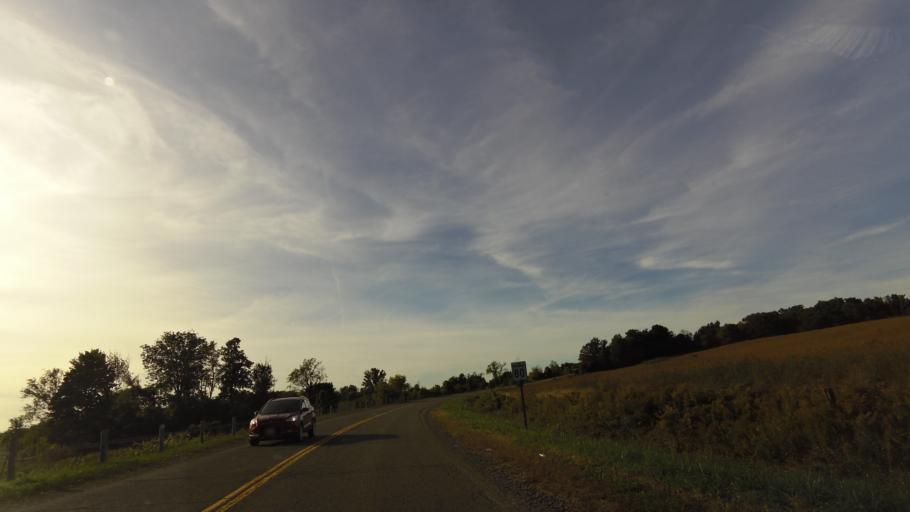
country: CA
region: Ontario
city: Ancaster
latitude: 43.1646
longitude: -79.9498
